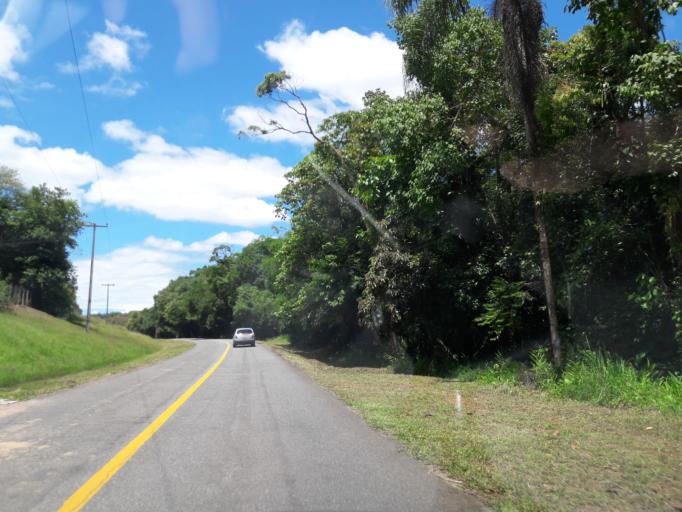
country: BR
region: Parana
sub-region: Antonina
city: Antonina
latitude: -25.4145
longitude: -48.8356
